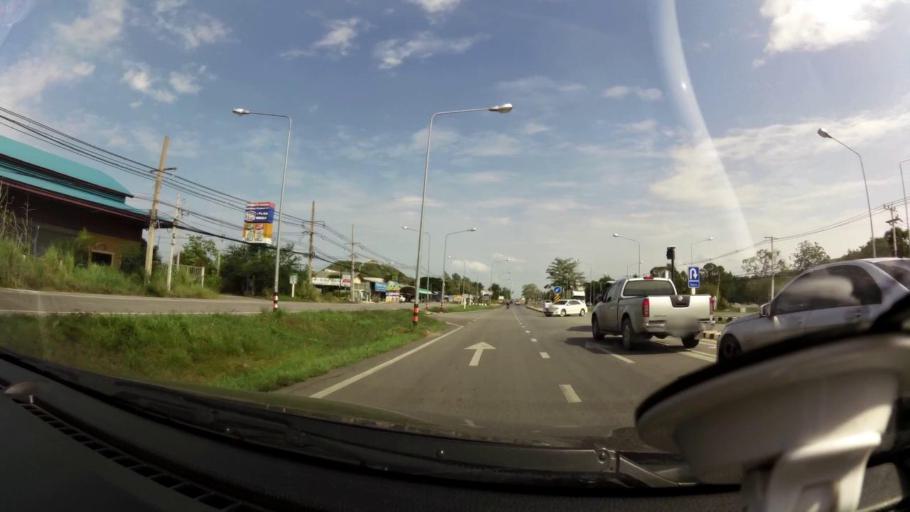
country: TH
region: Prachuap Khiri Khan
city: Hua Hin
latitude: 12.5290
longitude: 99.9618
